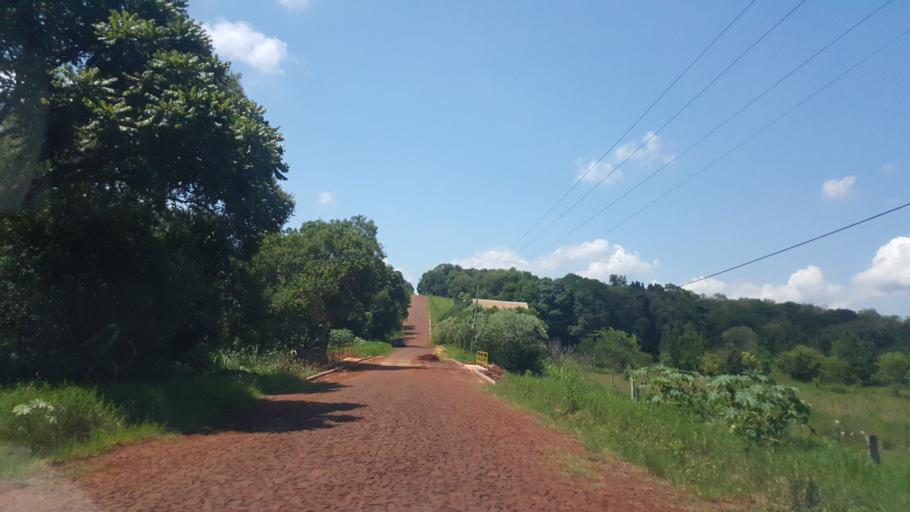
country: AR
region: Misiones
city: Capiovi
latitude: -26.9244
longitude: -55.0523
